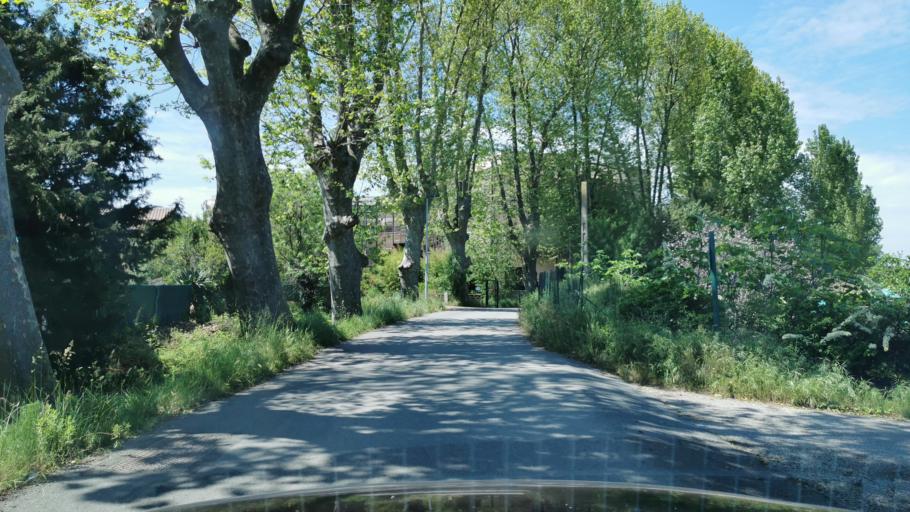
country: FR
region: Languedoc-Roussillon
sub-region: Departement de l'Aude
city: Narbonne
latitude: 43.1919
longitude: 3.0016
